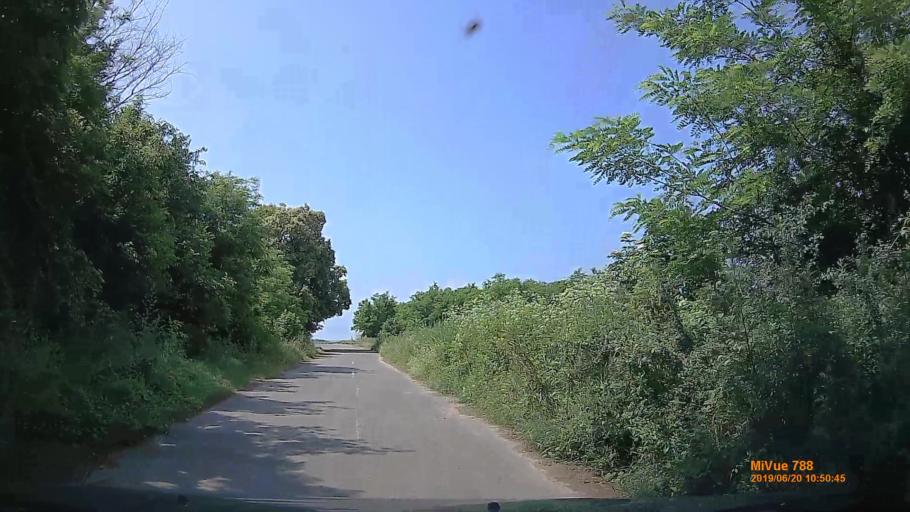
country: HU
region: Baranya
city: Mecseknadasd
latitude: 46.1589
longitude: 18.5820
